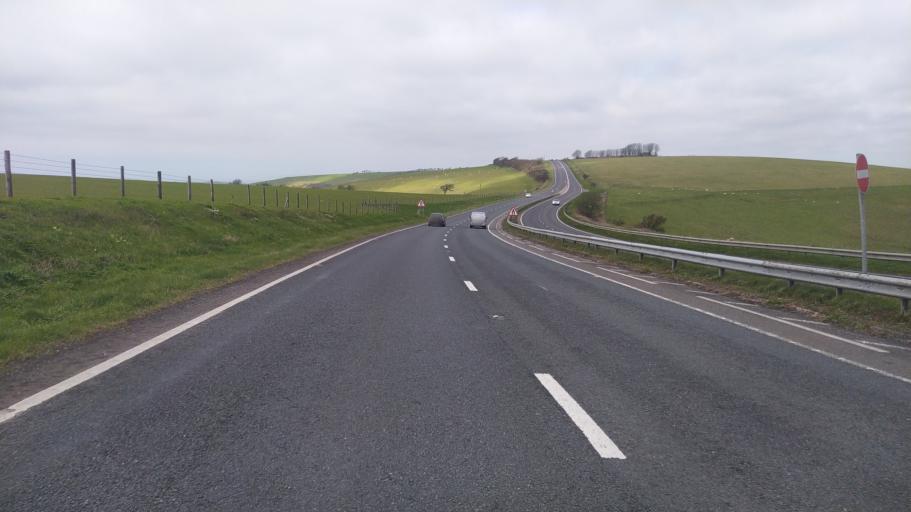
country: GB
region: England
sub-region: Dorset
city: Bridport
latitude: 50.7240
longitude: -2.6429
